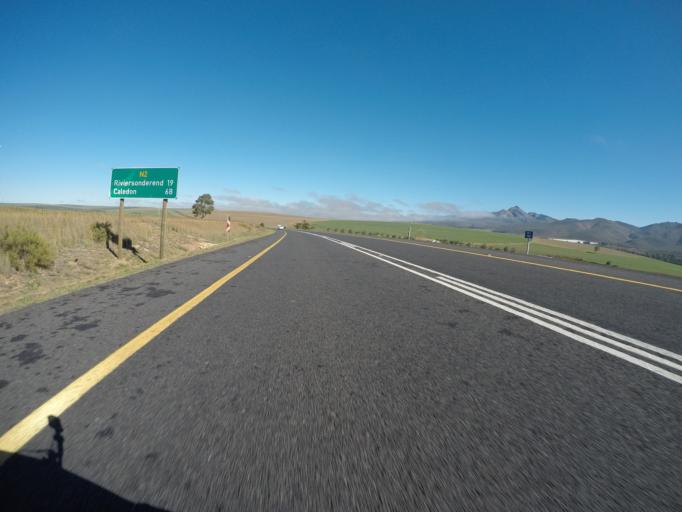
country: ZA
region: Western Cape
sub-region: Cape Winelands District Municipality
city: Ashton
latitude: -34.0902
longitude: 20.0832
